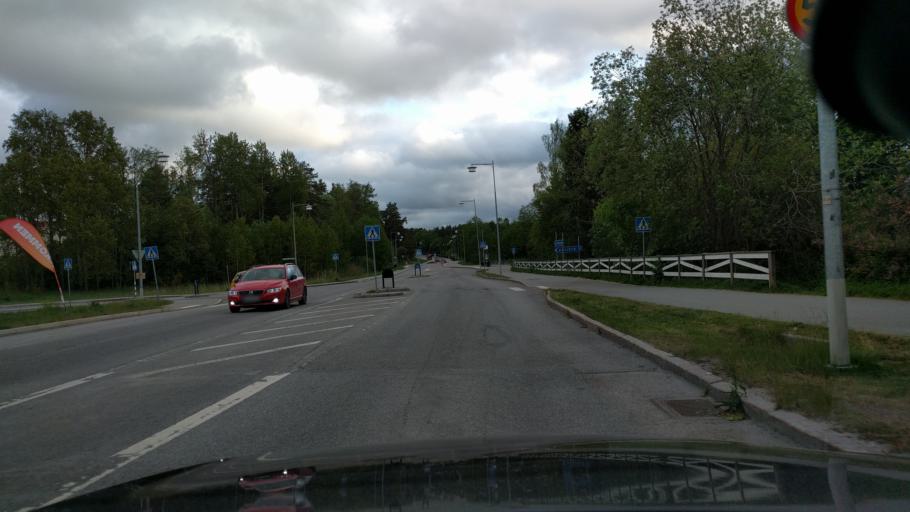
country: SE
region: Stockholm
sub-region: Vallentuna Kommun
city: Vallentuna
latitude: 59.5179
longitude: 18.0719
